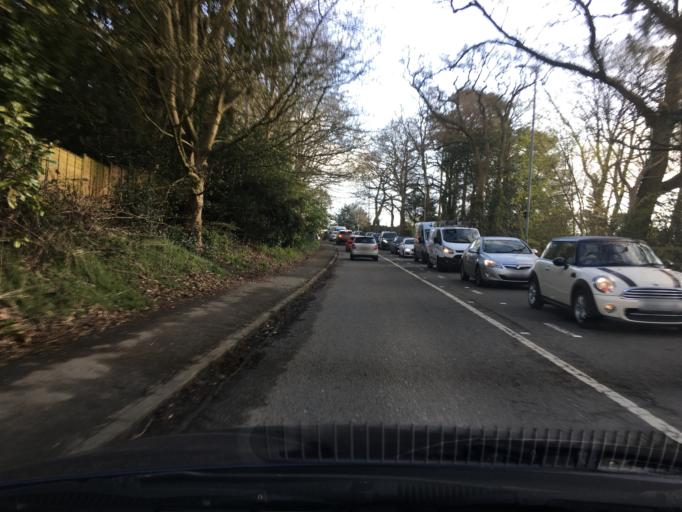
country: GB
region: England
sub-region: Bracknell Forest
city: Sandhurst
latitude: 51.3512
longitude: -0.7999
